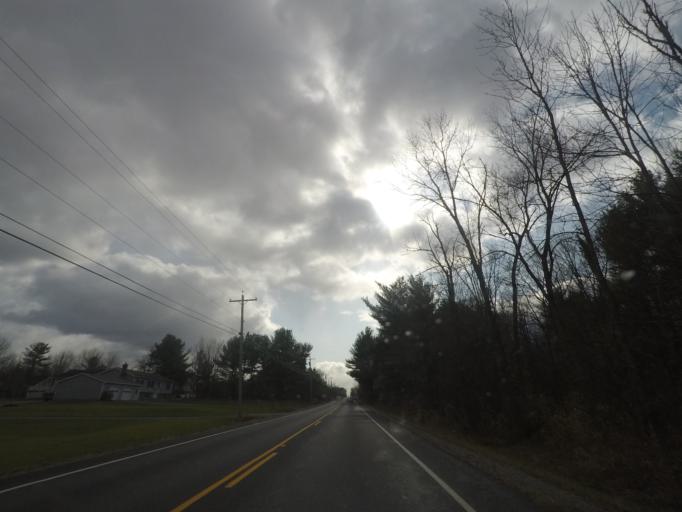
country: US
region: New York
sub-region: Saratoga County
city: Ballston Spa
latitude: 42.9678
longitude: -73.8305
